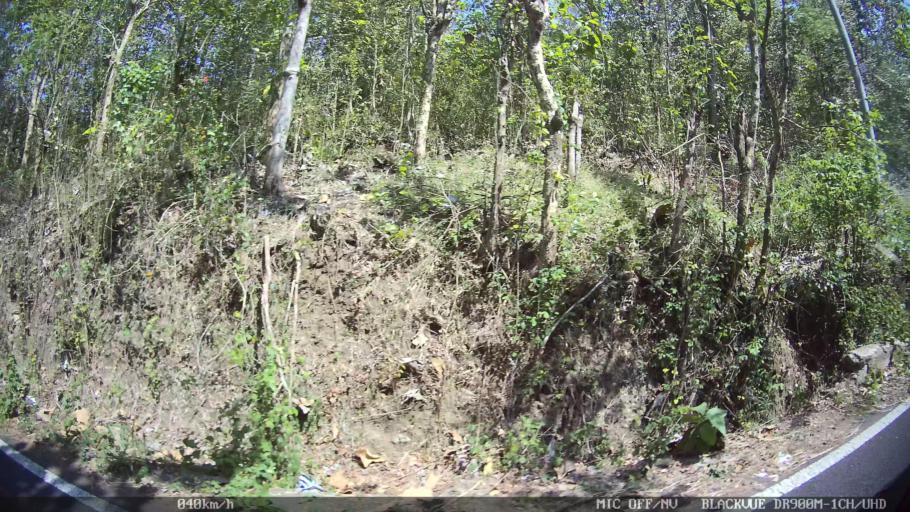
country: ID
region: Daerah Istimewa Yogyakarta
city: Pundong
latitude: -7.9571
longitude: 110.3675
